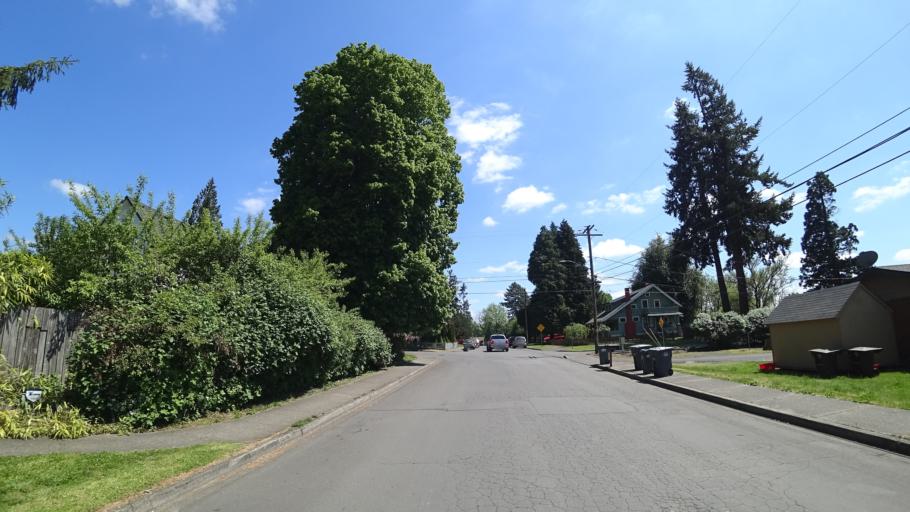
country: US
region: Oregon
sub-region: Washington County
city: Hillsboro
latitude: 45.5150
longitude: -122.9868
